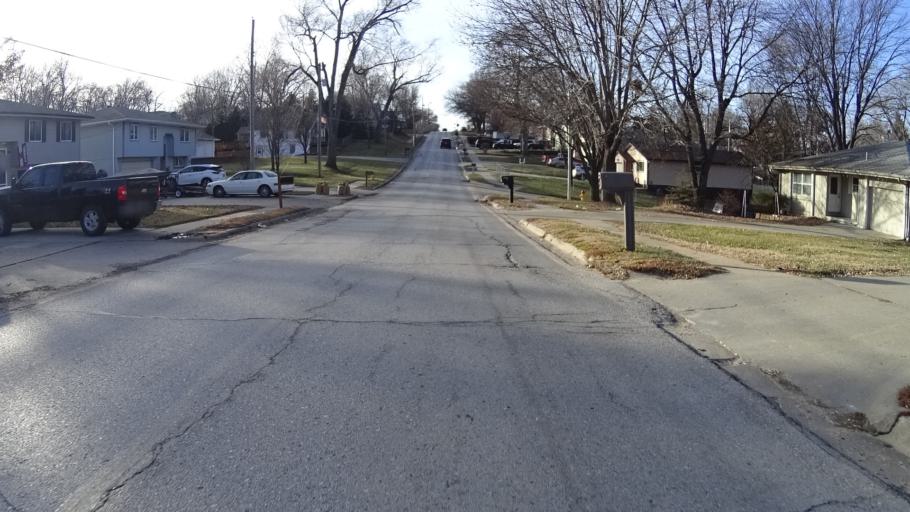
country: US
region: Nebraska
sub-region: Douglas County
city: Omaha
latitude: 41.1909
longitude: -95.9594
